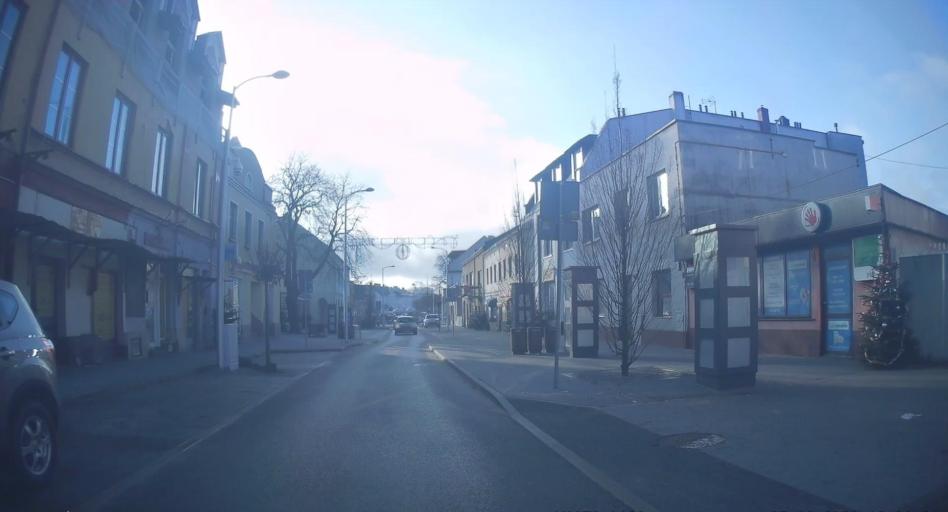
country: PL
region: Lodz Voivodeship
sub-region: Powiat rawski
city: Rawa Mazowiecka
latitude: 51.7651
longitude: 20.2524
